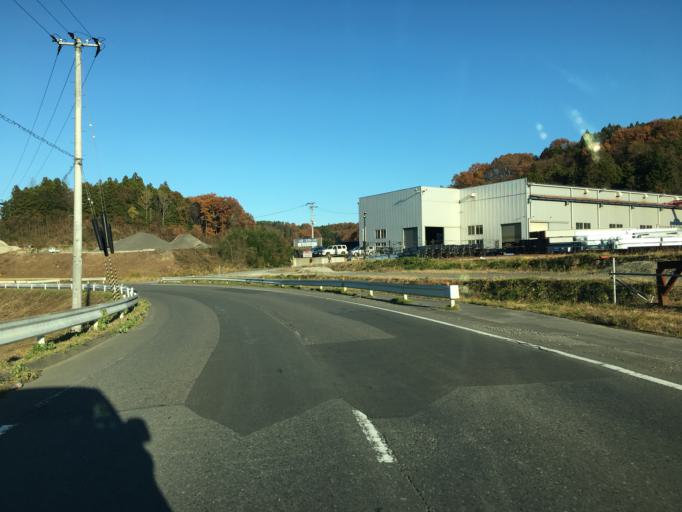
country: JP
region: Fukushima
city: Sukagawa
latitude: 37.3221
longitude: 140.4393
